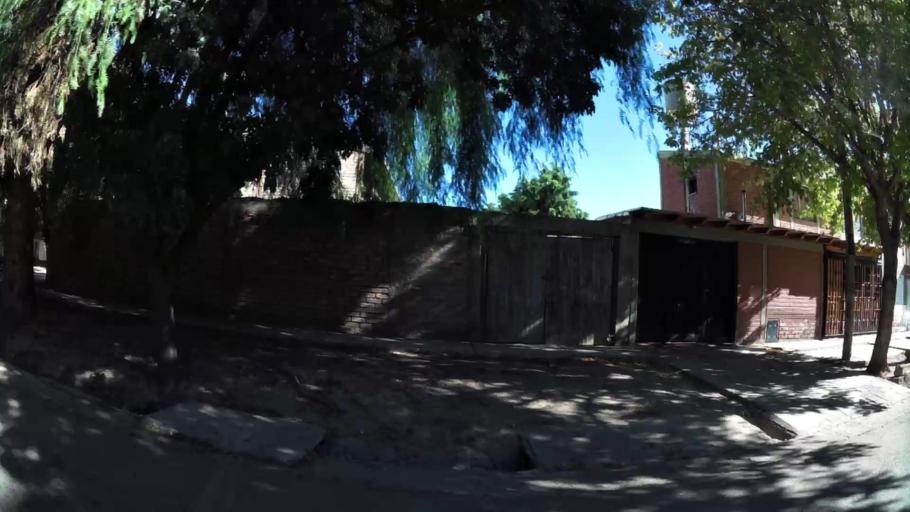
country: AR
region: Mendoza
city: Las Heras
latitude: -32.8519
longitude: -68.8293
